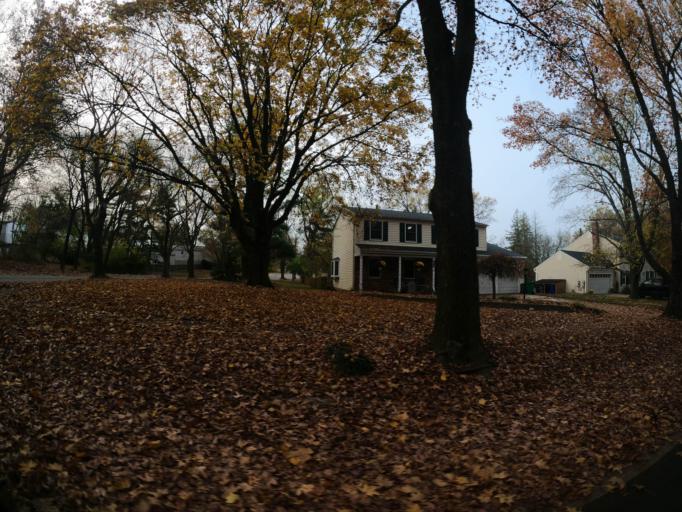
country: US
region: Maryland
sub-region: Howard County
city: Columbia
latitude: 39.2286
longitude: -76.8379
